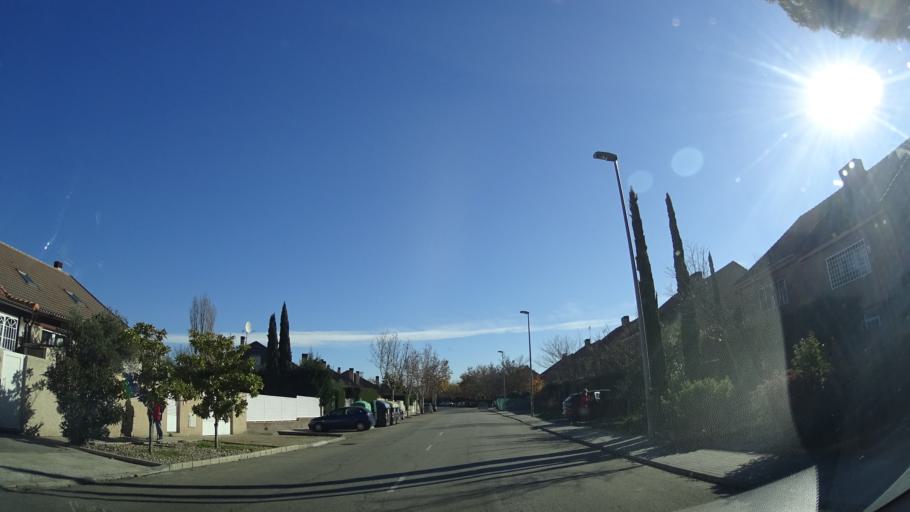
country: ES
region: Madrid
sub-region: Provincia de Madrid
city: Las Matas
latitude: 40.5216
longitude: -3.9113
